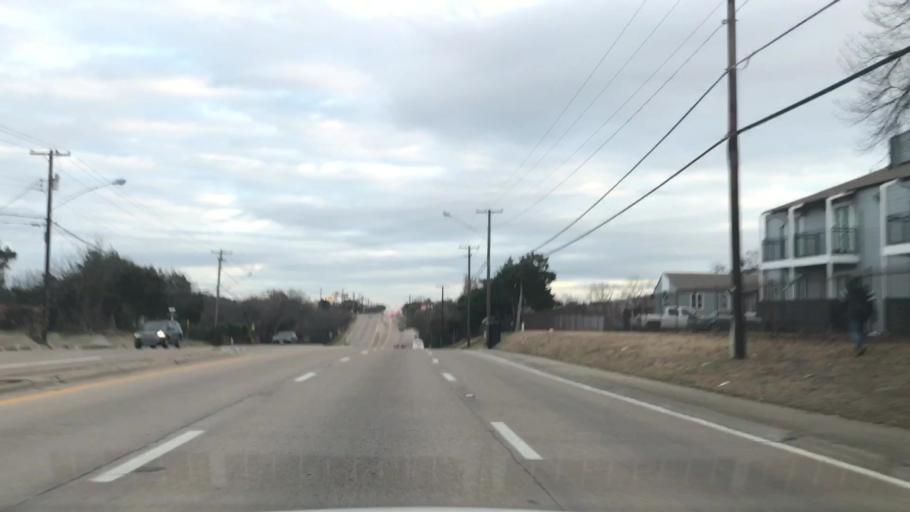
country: US
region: Texas
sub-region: Dallas County
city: Cockrell Hill
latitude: 32.6912
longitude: -96.8637
